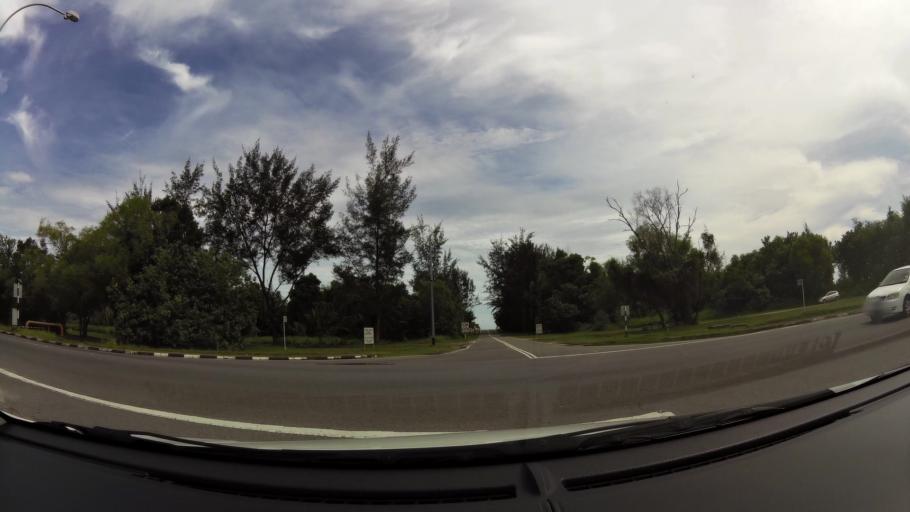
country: BN
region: Belait
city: Seria
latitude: 4.6093
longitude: 114.3114
